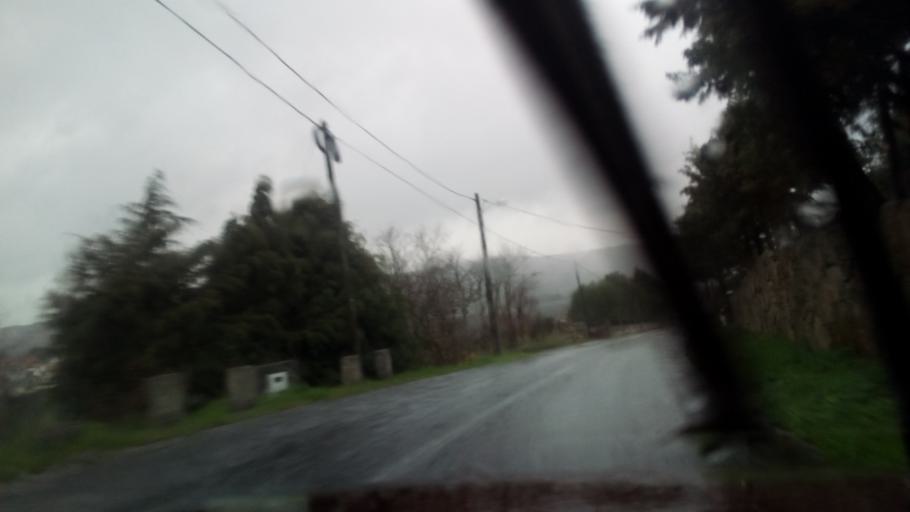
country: PT
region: Guarda
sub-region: Celorico da Beira
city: Celorico da Beira
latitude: 40.6265
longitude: -7.4329
